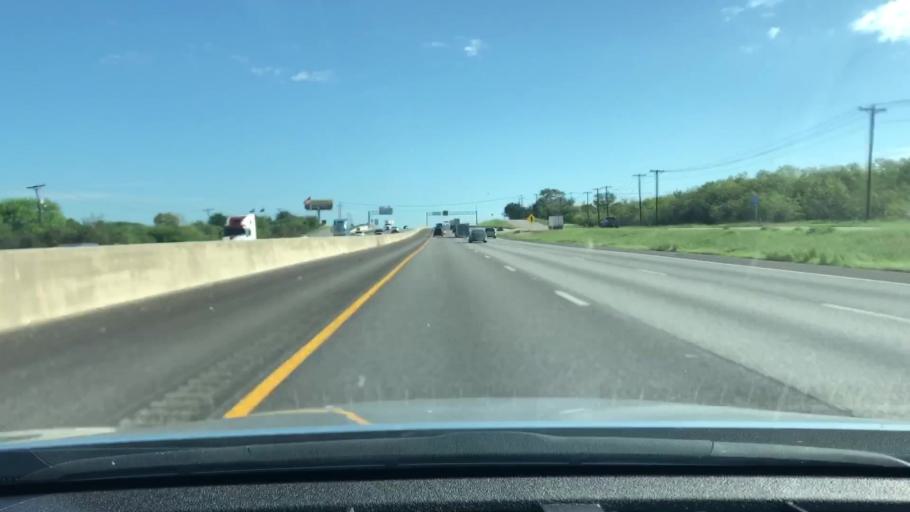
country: US
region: Texas
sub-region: Guadalupe County
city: Lake Dunlap
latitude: 29.7411
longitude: -98.0638
